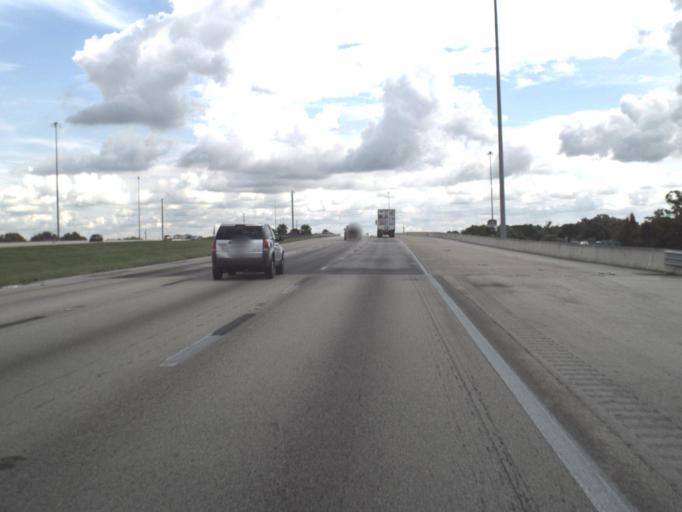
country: US
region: Florida
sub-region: Polk County
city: Gibsonia
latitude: 28.0828
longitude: -81.9730
